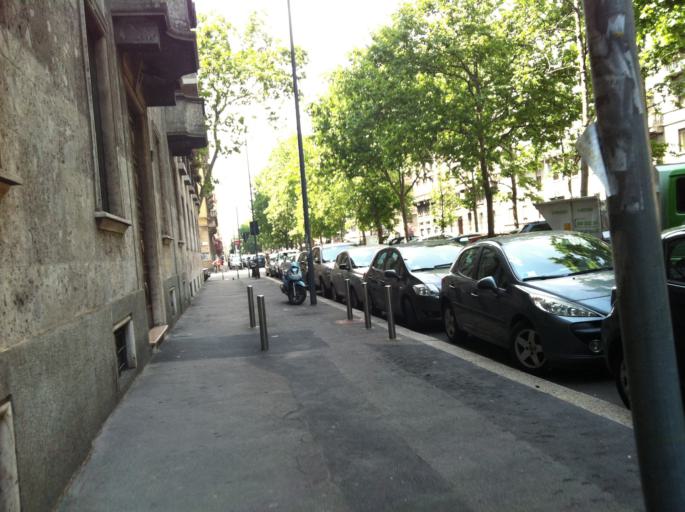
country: IT
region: Lombardy
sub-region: Citta metropolitana di Milano
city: Milano
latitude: 45.4720
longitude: 9.2167
